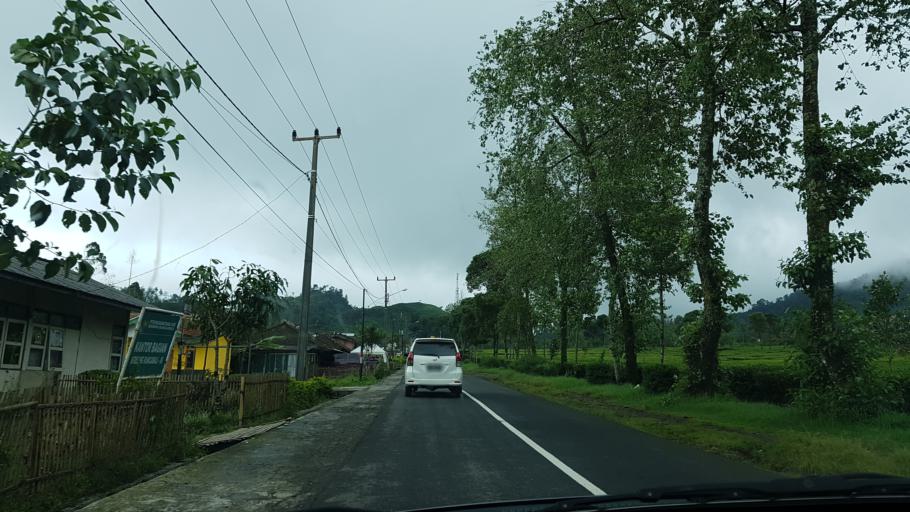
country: ID
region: West Java
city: Banjar
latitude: -7.1537
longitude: 107.3726
